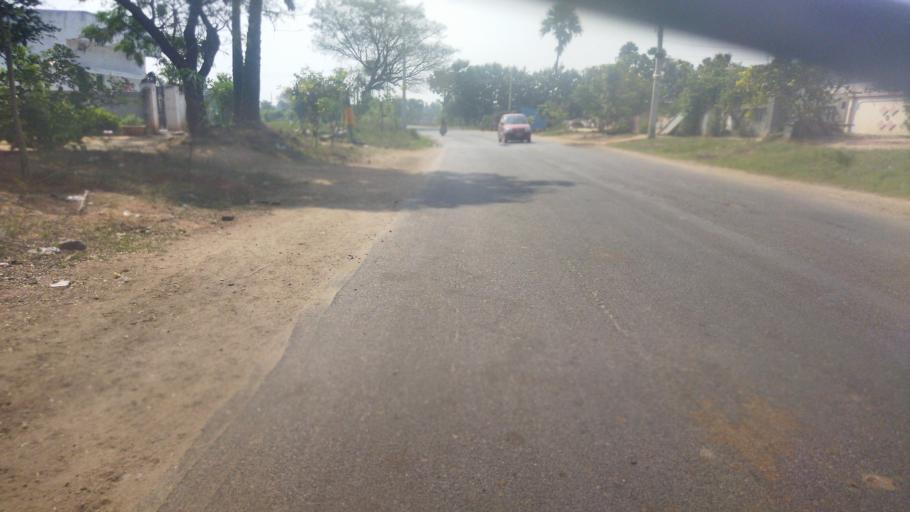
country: IN
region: Telangana
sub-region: Nalgonda
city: Nalgonda
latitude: 17.1475
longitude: 79.3102
